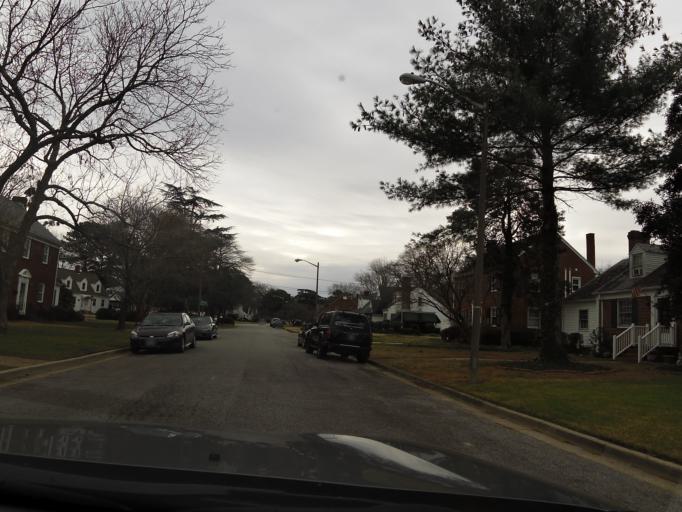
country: US
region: Virginia
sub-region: City of Portsmouth
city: Portsmouth Heights
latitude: 36.8363
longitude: -76.3535
